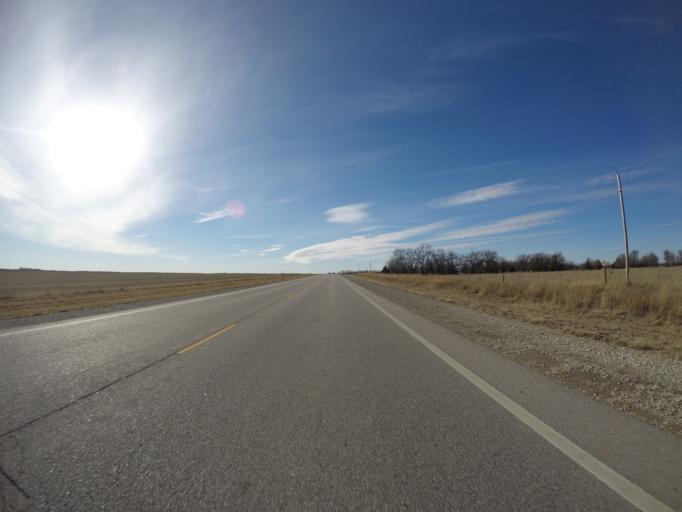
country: US
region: Kansas
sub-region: Marion County
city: Hillsboro
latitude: 38.3771
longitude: -97.3960
